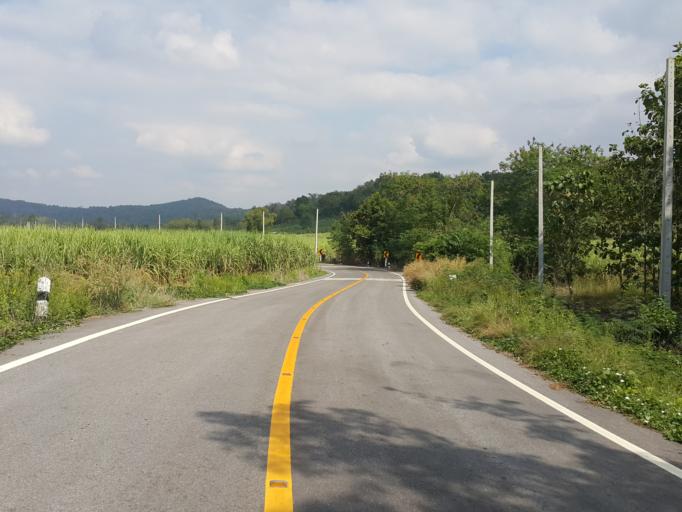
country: TH
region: Sukhothai
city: Thung Saliam
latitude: 17.4459
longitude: 99.5879
